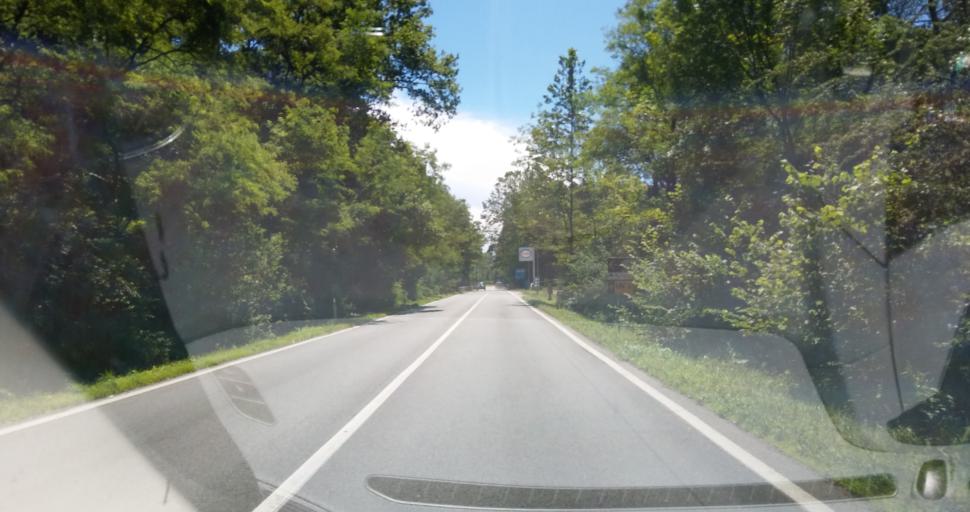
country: IT
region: Lombardy
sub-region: Provincia di Varese
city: Vergiate
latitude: 45.7078
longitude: 8.6971
